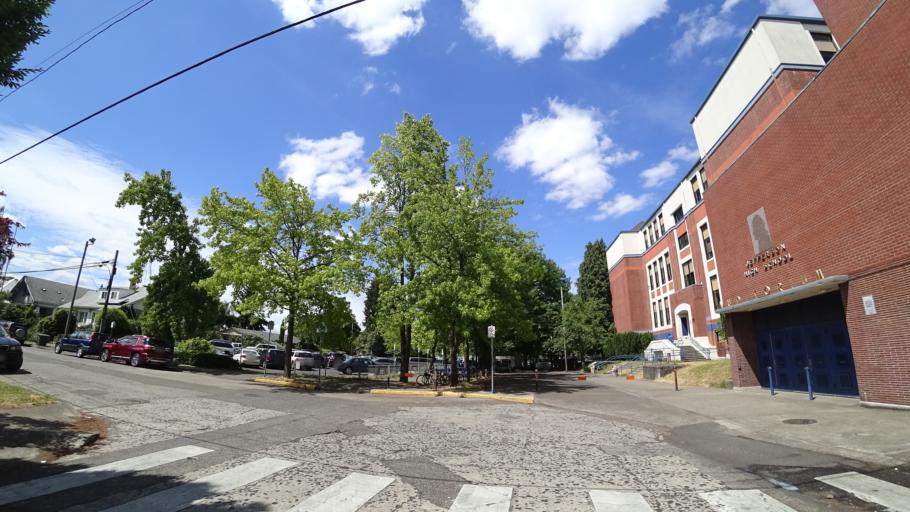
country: US
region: Oregon
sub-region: Multnomah County
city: Portland
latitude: 45.5603
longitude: -122.6730
